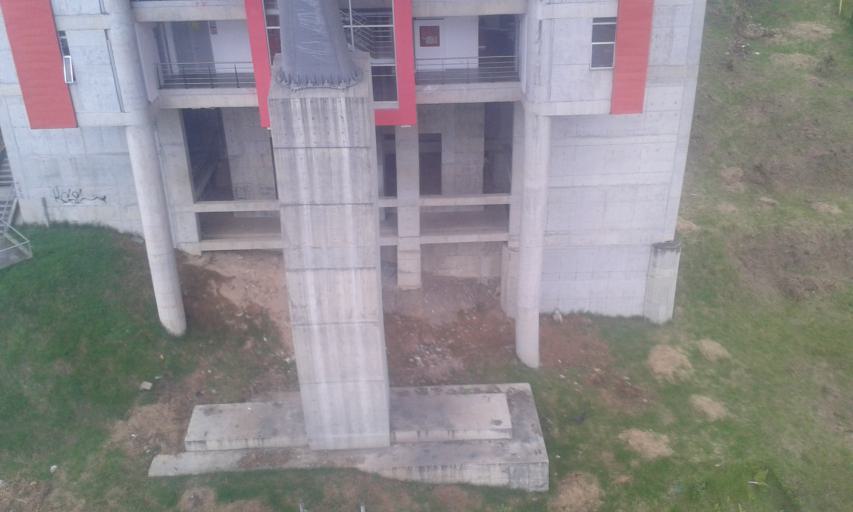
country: CO
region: Caldas
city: Manizales
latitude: 5.0578
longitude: -75.5088
